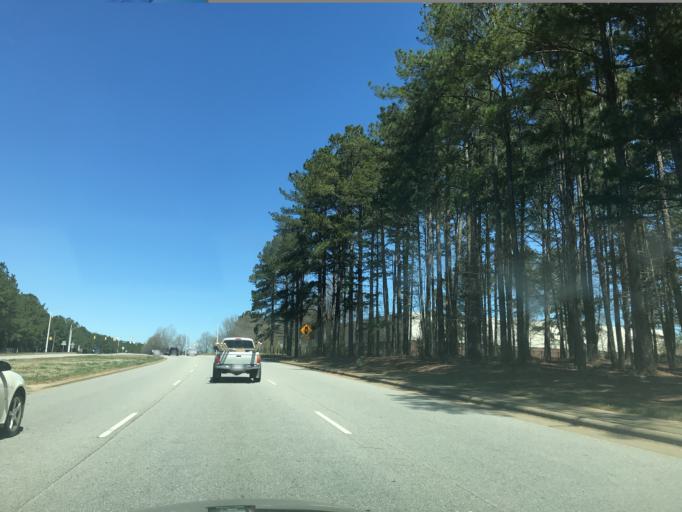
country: US
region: North Carolina
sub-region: Wake County
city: Garner
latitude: 35.7230
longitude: -78.6385
